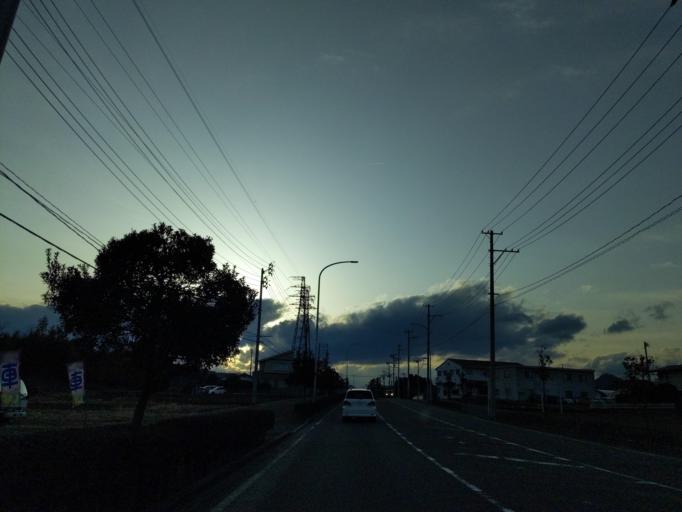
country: JP
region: Miyagi
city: Sendai
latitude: 38.2135
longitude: 140.8472
